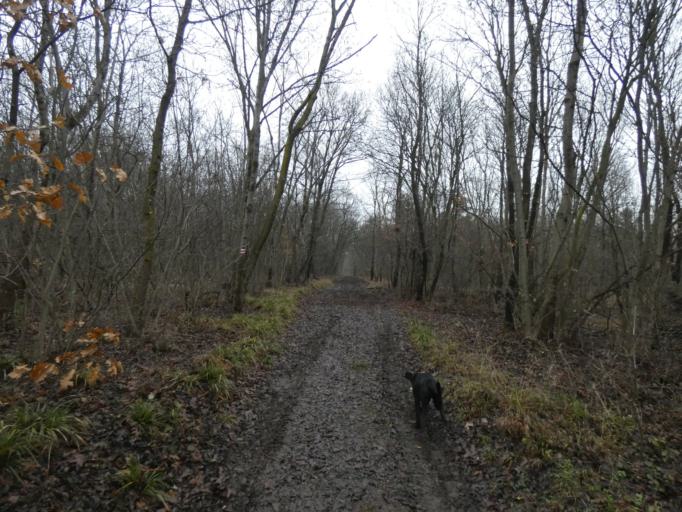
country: HU
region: Pest
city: Soskut
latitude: 47.4383
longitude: 18.8429
